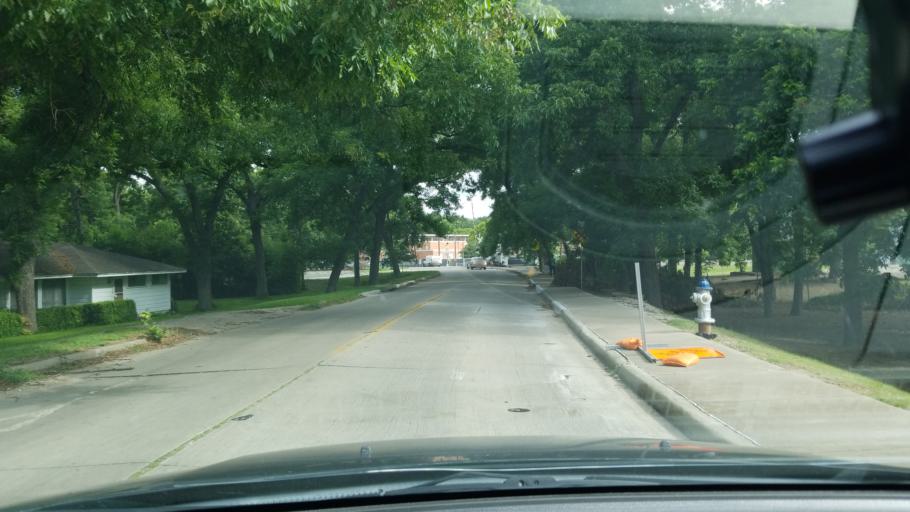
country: US
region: Texas
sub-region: Dallas County
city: Highland Park
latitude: 32.8113
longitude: -96.7091
